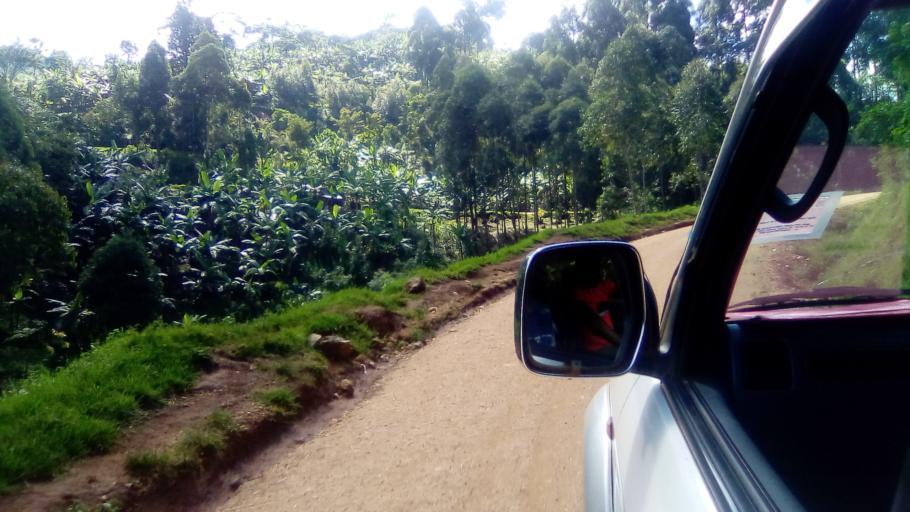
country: UG
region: Eastern Region
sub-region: Mbale District
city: Mbale
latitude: 1.0609
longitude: 34.2404
